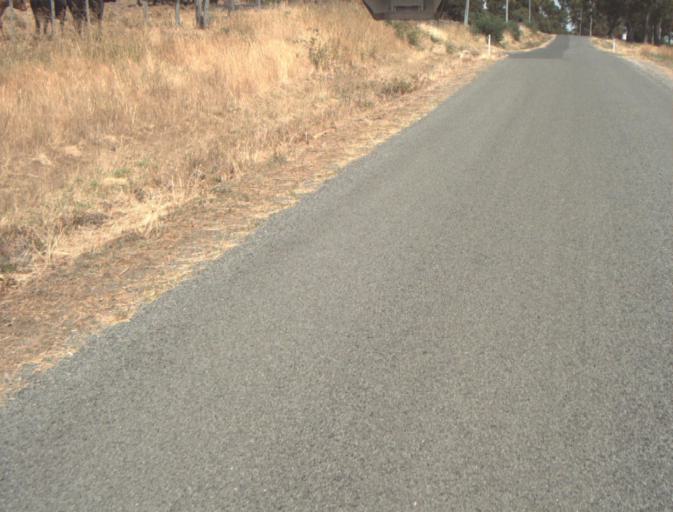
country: AU
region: Tasmania
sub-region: Launceston
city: Newstead
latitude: -41.4968
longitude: 147.2132
